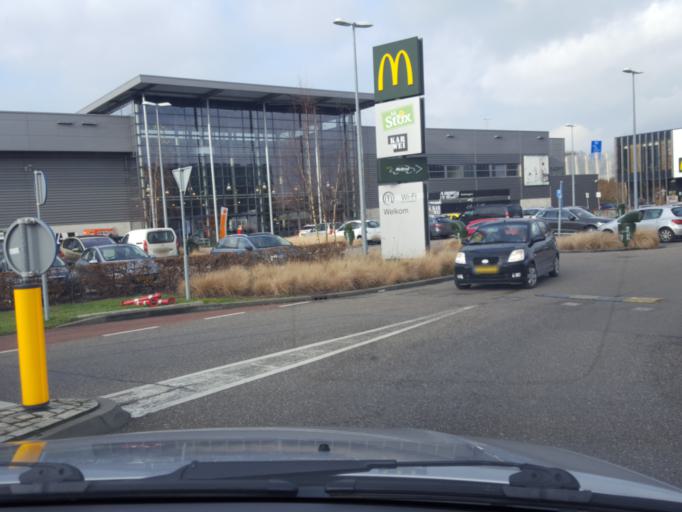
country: NL
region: Limburg
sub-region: Gemeente Venlo
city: Tegelen
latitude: 51.3509
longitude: 6.1520
